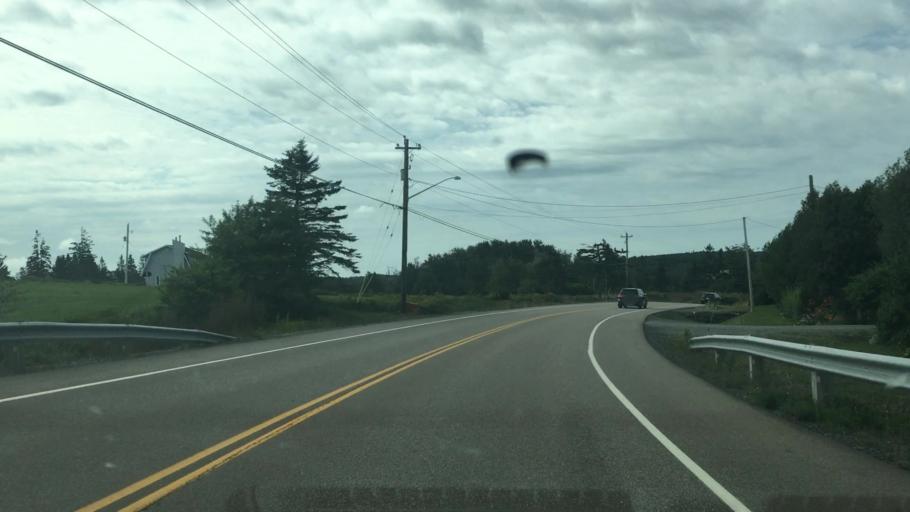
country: CA
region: Nova Scotia
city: Princeville
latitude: 45.6956
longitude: -60.7364
